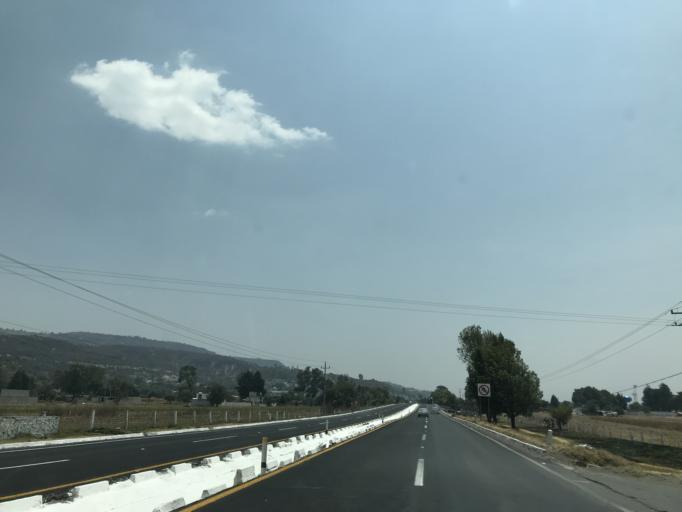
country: MX
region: Tlaxcala
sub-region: Panotla
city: San Francisco Temetzontla
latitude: 19.3265
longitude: -98.3163
